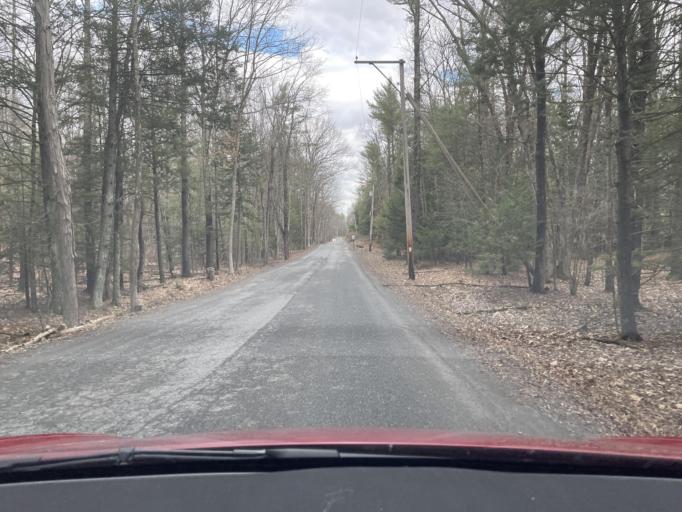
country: US
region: New York
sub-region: Ulster County
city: Zena
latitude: 42.0668
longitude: -74.0354
